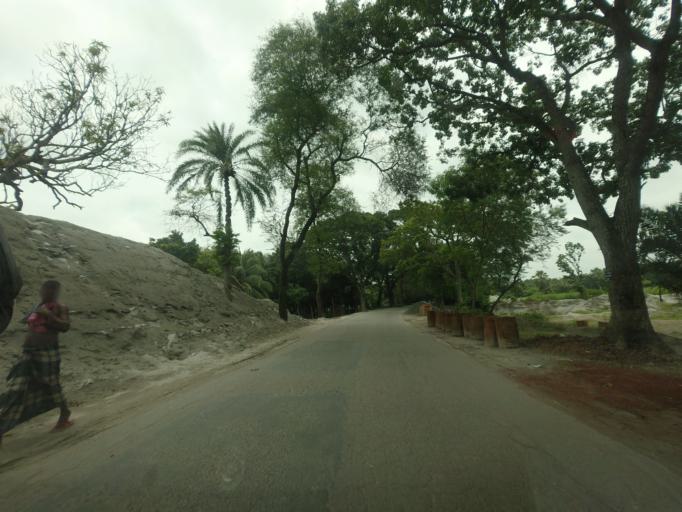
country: BD
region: Khulna
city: Kalia
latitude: 23.2069
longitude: 89.6997
